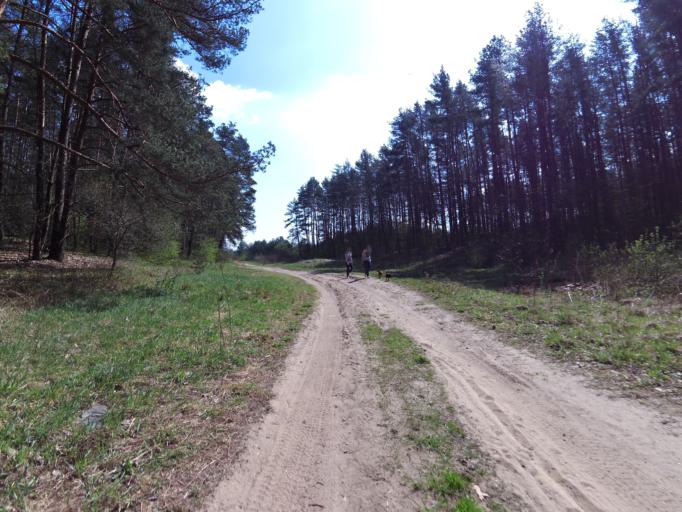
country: LT
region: Vilnius County
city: Pilaite
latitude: 54.6990
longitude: 25.2001
